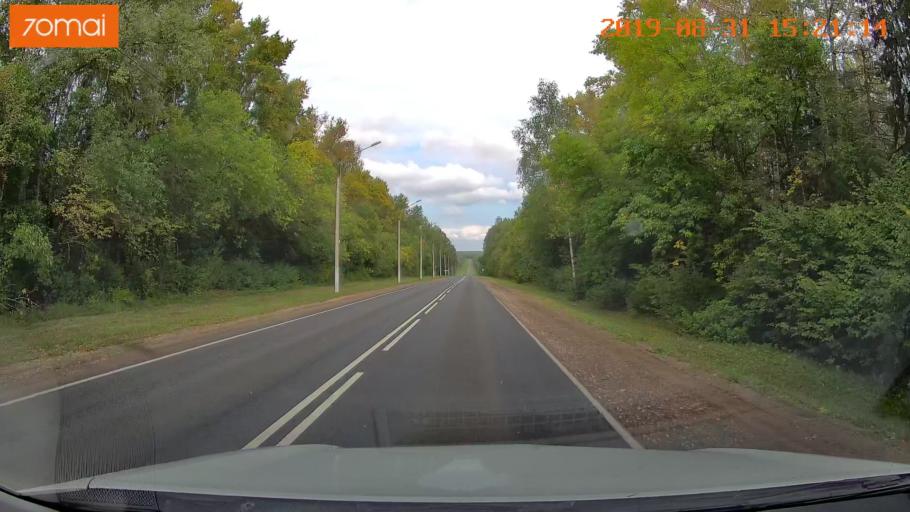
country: RU
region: Kaluga
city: Baryatino
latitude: 54.4949
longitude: 34.4498
